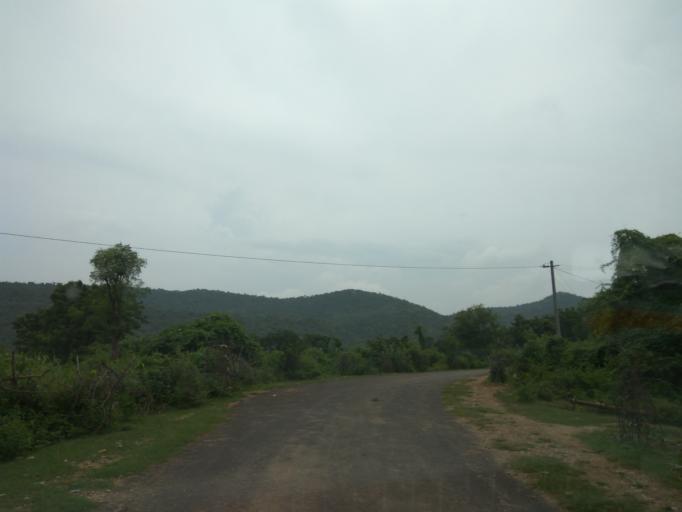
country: IN
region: Andhra Pradesh
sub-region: Prakasam
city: Cumbum
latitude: 15.4486
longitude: 79.0795
